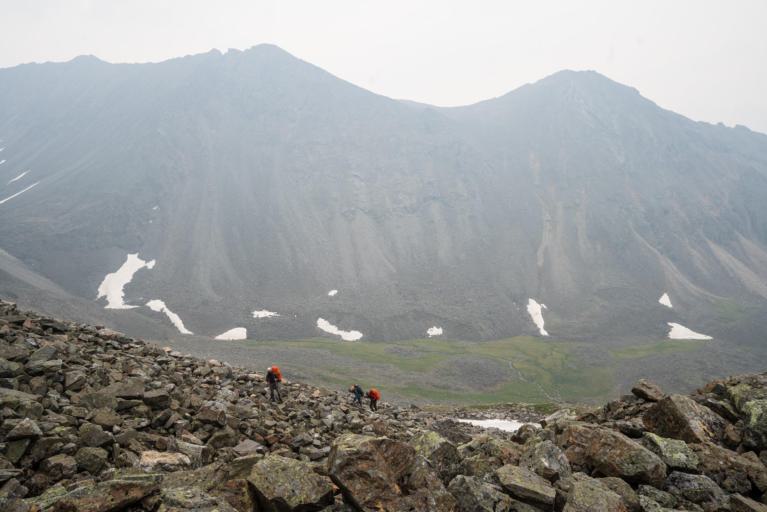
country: RU
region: Transbaikal Territory
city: Kuanda
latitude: 56.8066
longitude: 117.1174
